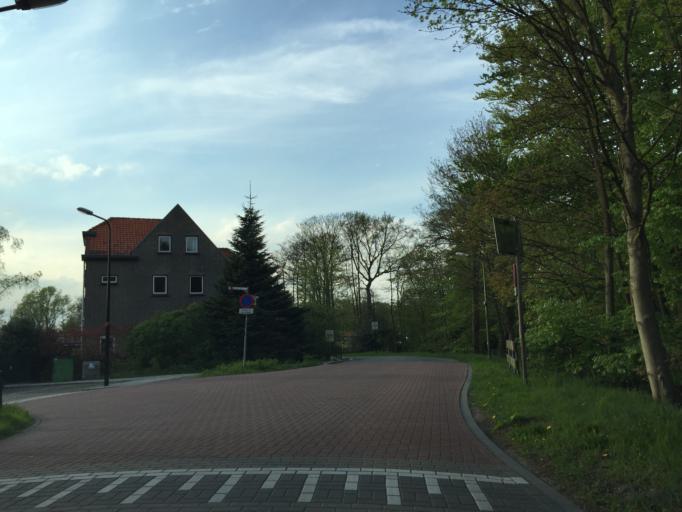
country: NL
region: South Holland
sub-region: Gemeente Leidschendam-Voorburg
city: Voorburg
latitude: 52.1034
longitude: 4.3424
